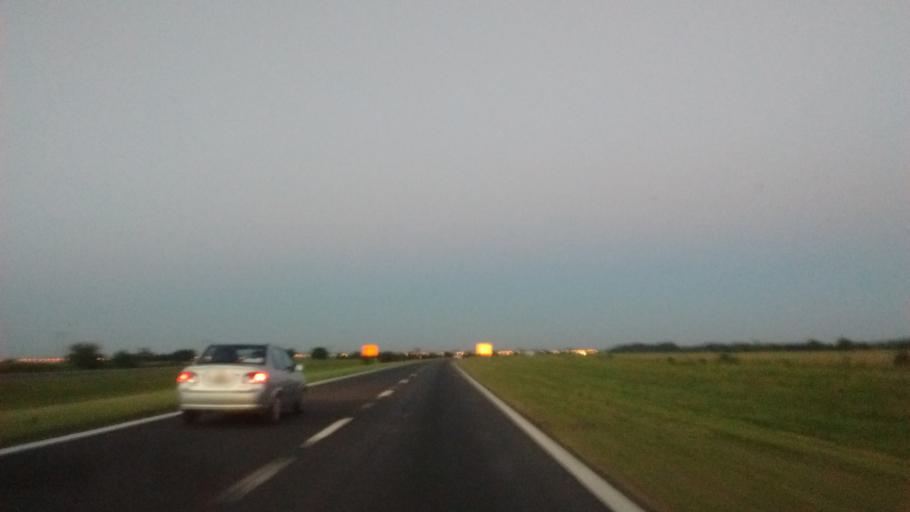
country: AR
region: Santa Fe
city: Funes
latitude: -32.9337
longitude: -60.8478
